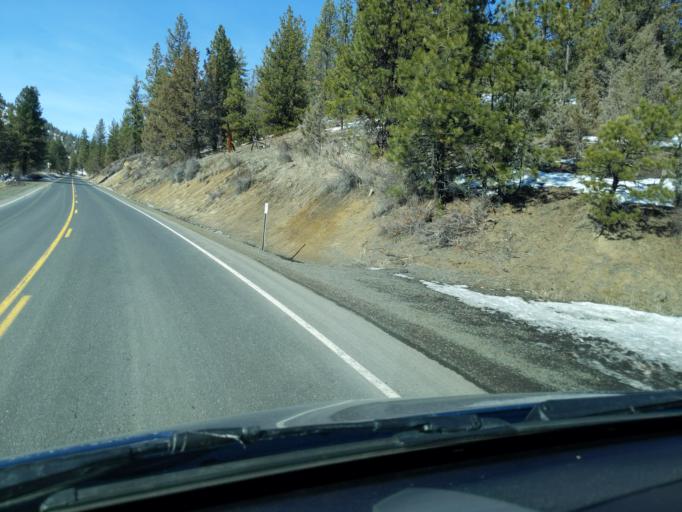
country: US
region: Oregon
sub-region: Grant County
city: John Day
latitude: 44.8898
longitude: -119.0108
